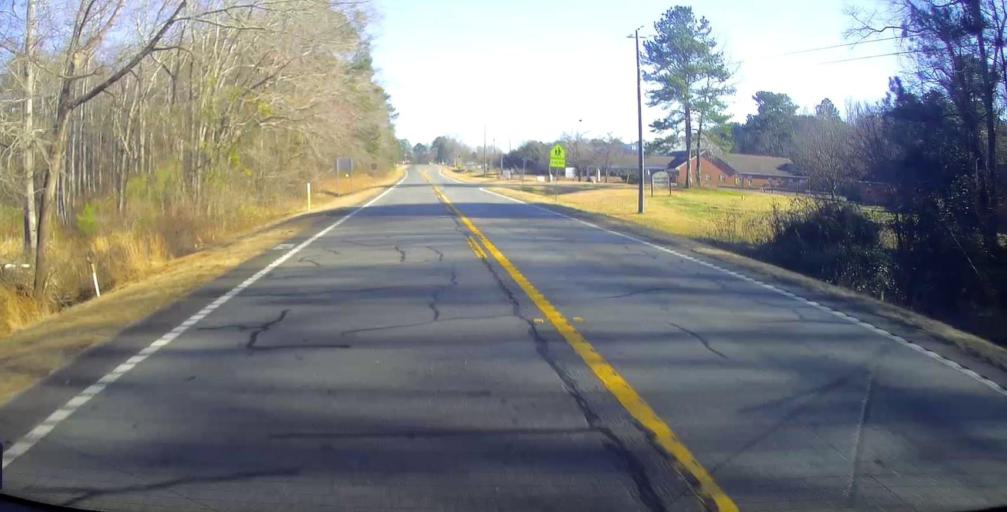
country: US
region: Georgia
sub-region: Talbot County
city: Talbotton
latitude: 32.6928
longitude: -84.5451
